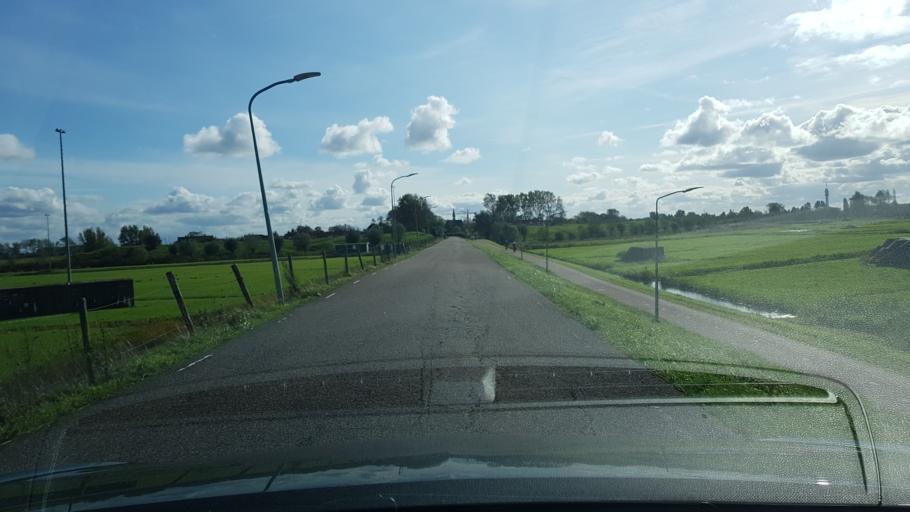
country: NL
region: North Holland
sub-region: Gemeente Velsen
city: Velsen-Zuid
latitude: 52.4191
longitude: 4.6738
